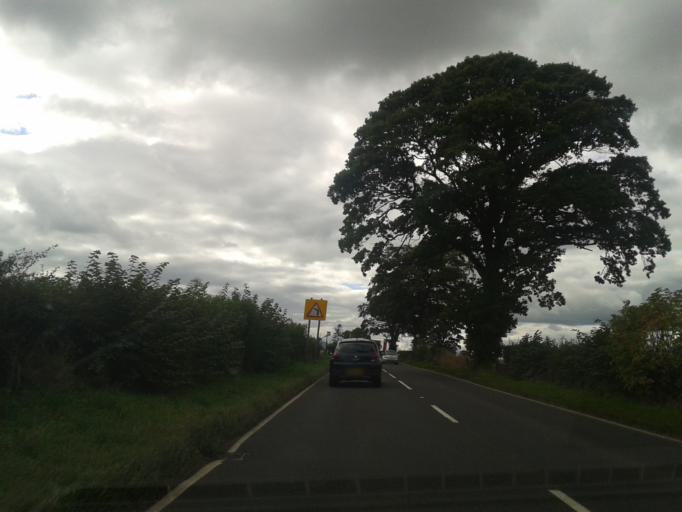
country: GB
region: Scotland
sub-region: Fife
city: Cupar
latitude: 56.3102
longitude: -3.0654
